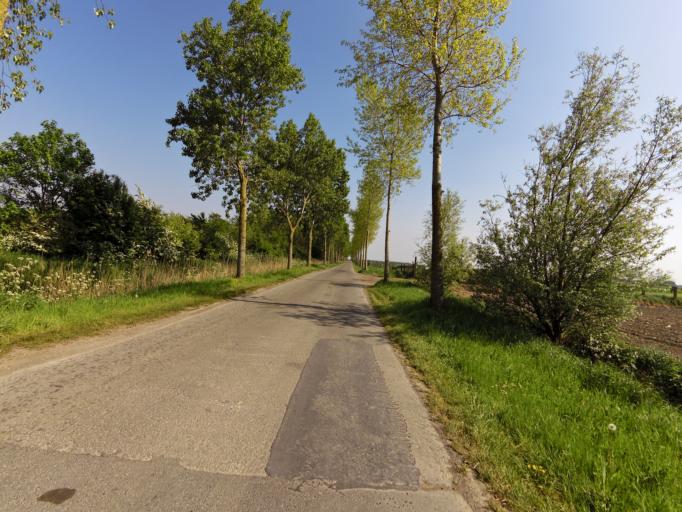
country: BE
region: Flanders
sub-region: Provincie West-Vlaanderen
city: Ostend
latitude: 51.1978
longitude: 2.9198
